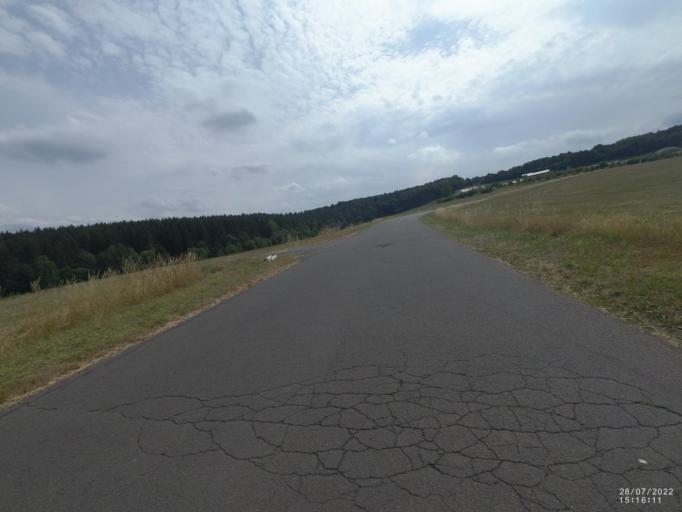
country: DE
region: Rheinland-Pfalz
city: Oberbettingen
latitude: 50.2659
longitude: 6.6435
